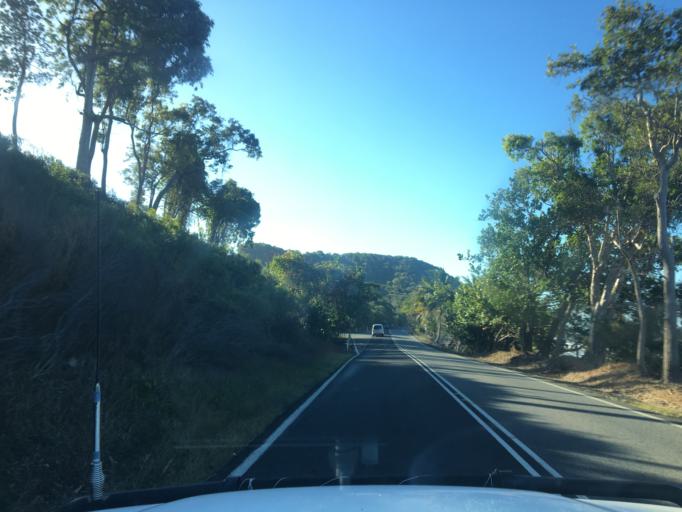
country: AU
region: Queensland
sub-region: Cairns
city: Port Douglas
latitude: -16.5825
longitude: 145.5126
